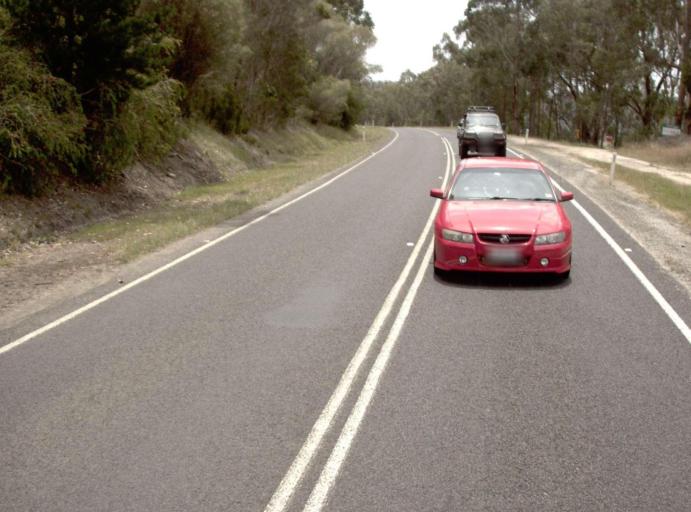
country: AU
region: Victoria
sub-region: Latrobe
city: Traralgon
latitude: -38.4557
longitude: 146.7373
